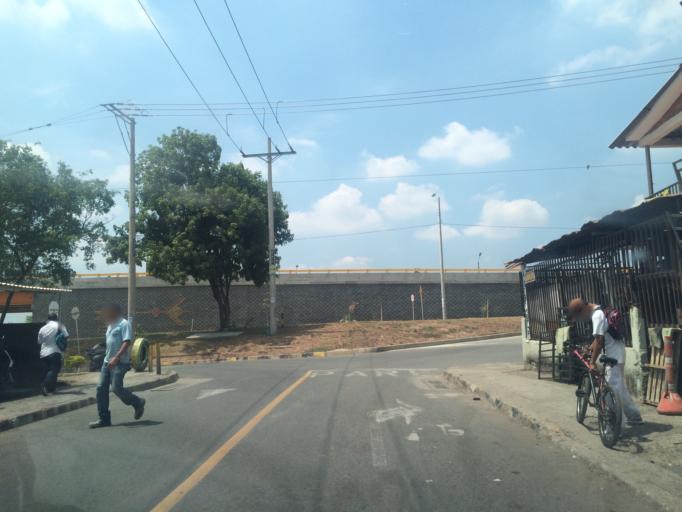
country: CO
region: Valle del Cauca
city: Cali
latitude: 3.4922
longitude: -76.4896
